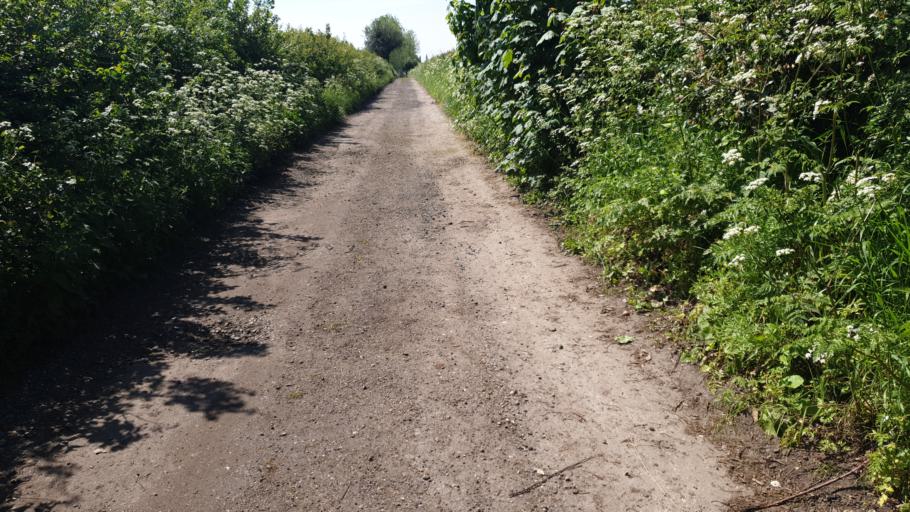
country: GB
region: England
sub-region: Essex
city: Manningtree
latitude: 51.9318
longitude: 1.0412
